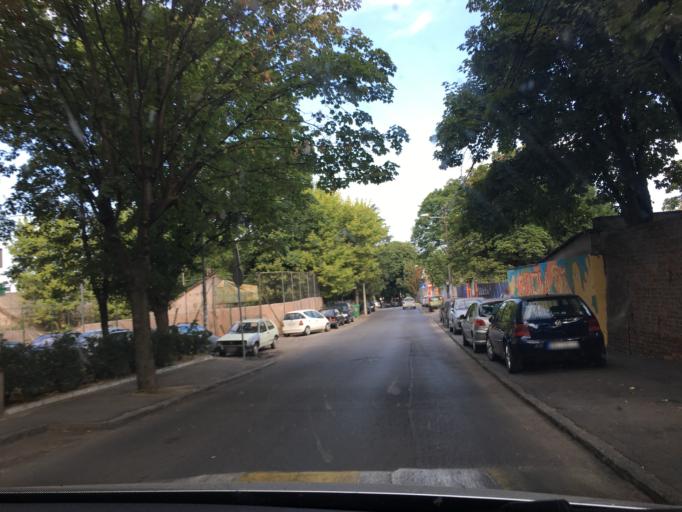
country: RS
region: Central Serbia
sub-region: Belgrade
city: Palilula
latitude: 44.7960
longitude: 20.5069
